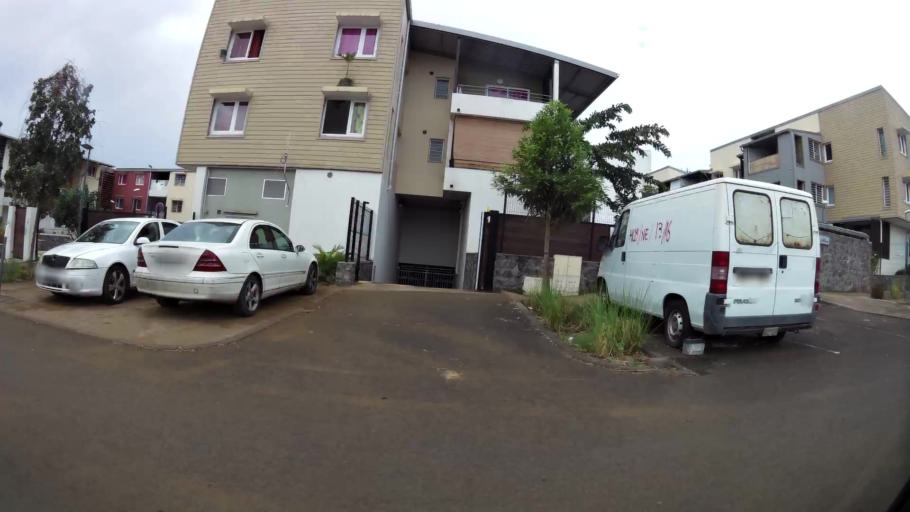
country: RE
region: Reunion
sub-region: Reunion
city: Sainte-Suzanne
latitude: -20.9015
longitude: 55.5975
